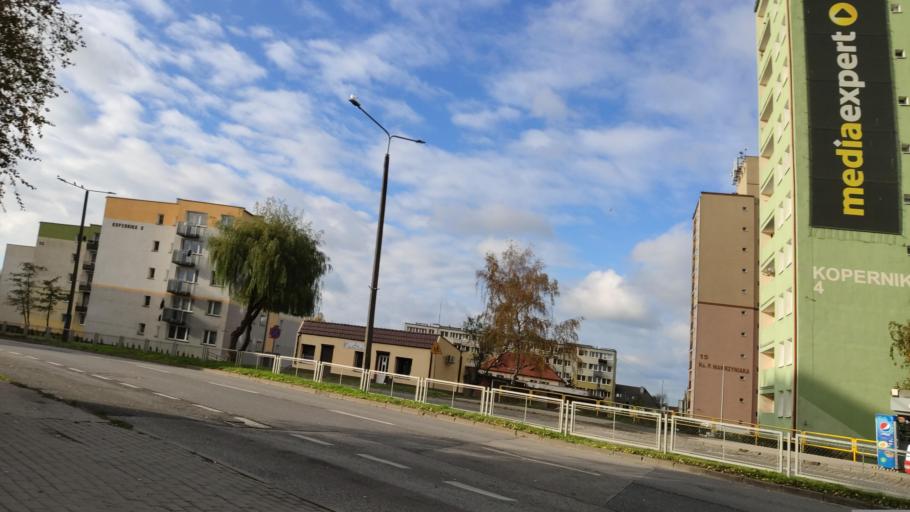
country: PL
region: Kujawsko-Pomorskie
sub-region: Powiat inowroclawski
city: Inowroclaw
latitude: 52.8014
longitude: 18.2510
